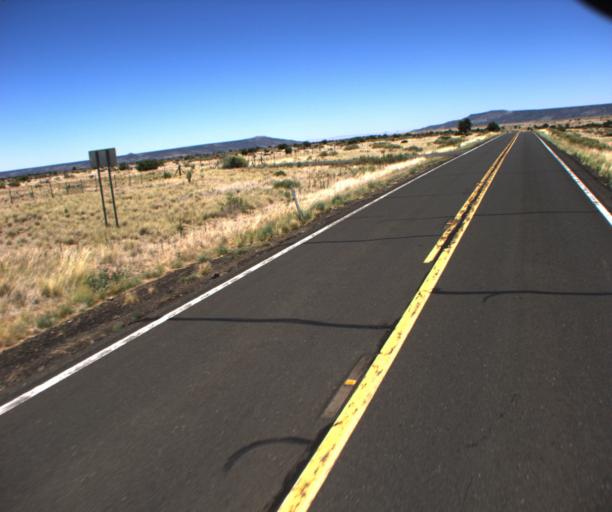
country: US
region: Arizona
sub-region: Coconino County
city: LeChee
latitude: 34.7624
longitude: -111.0188
